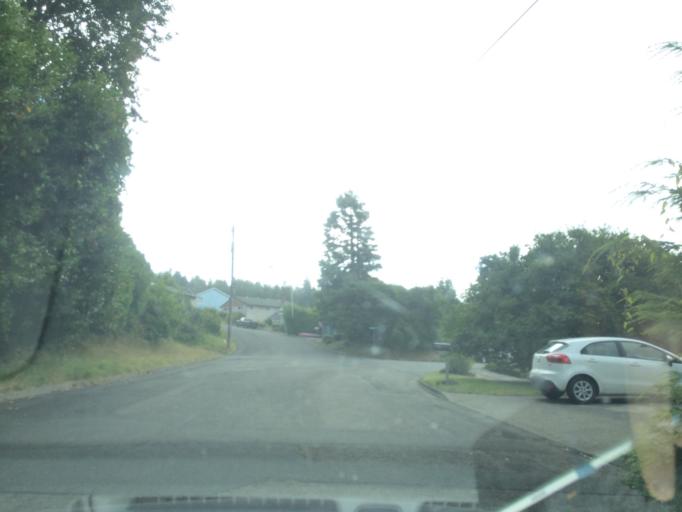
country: US
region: Oregon
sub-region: Clatsop County
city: Astoria
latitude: 46.1810
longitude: -123.8504
